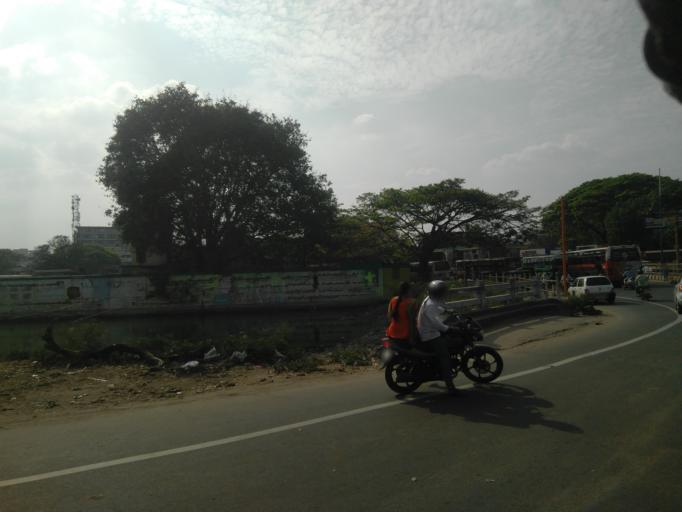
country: IN
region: Tamil Nadu
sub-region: Coimbatore
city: Coimbatore
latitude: 10.9982
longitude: 76.9851
